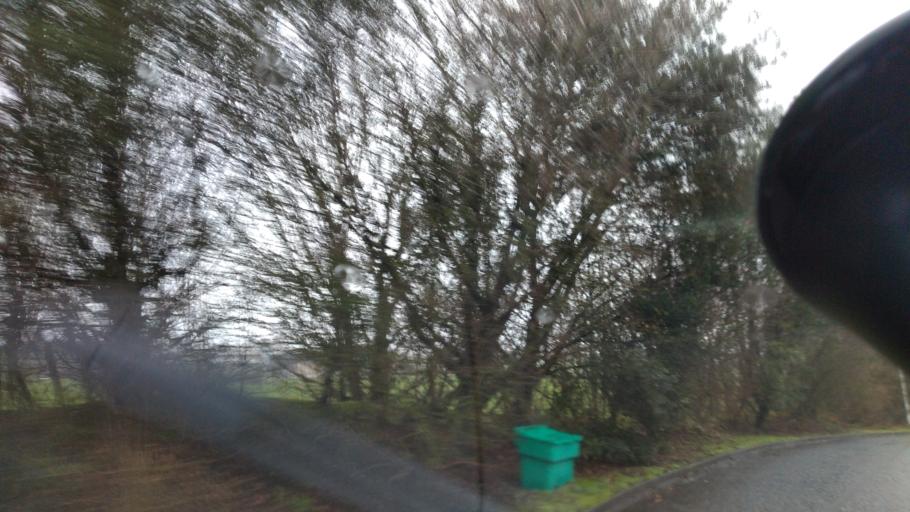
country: GB
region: England
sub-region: West Sussex
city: Arundel
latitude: 50.8423
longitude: -0.5405
